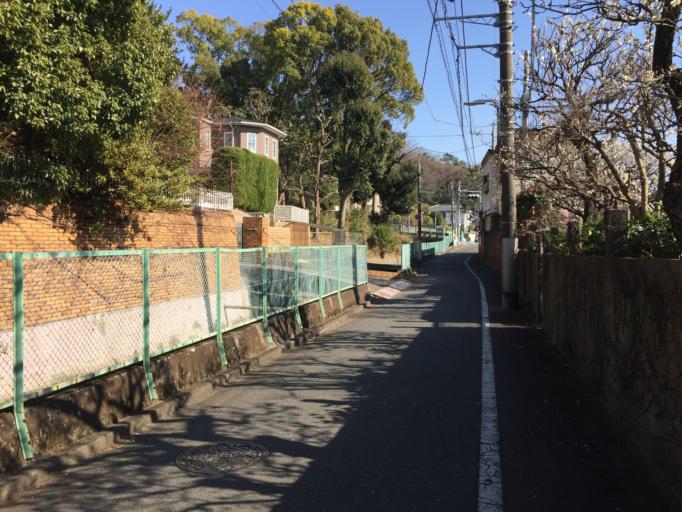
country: JP
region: Kanagawa
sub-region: Kawasaki-shi
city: Kawasaki
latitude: 35.5914
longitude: 139.6635
